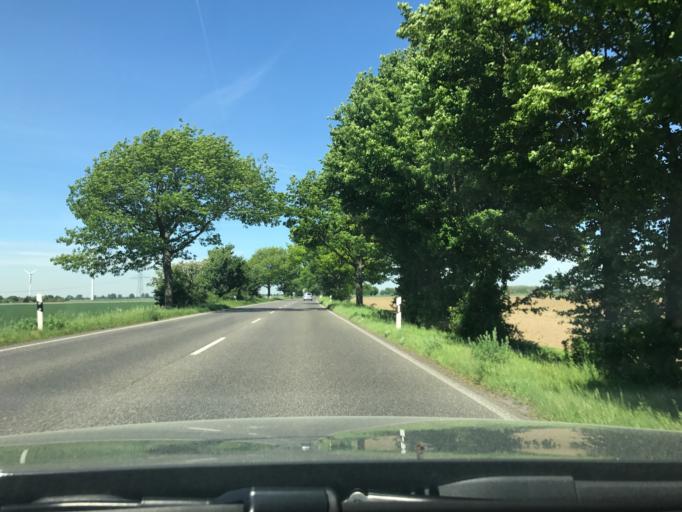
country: DE
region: North Rhine-Westphalia
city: Tonisvorst
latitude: 51.3557
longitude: 6.5103
